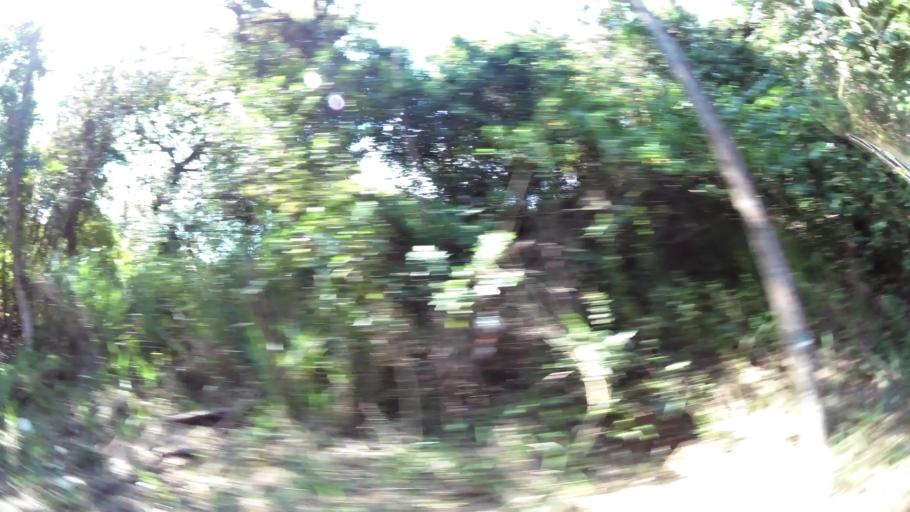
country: CO
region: Valle del Cauca
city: Cali
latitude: 3.4301
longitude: -76.5633
